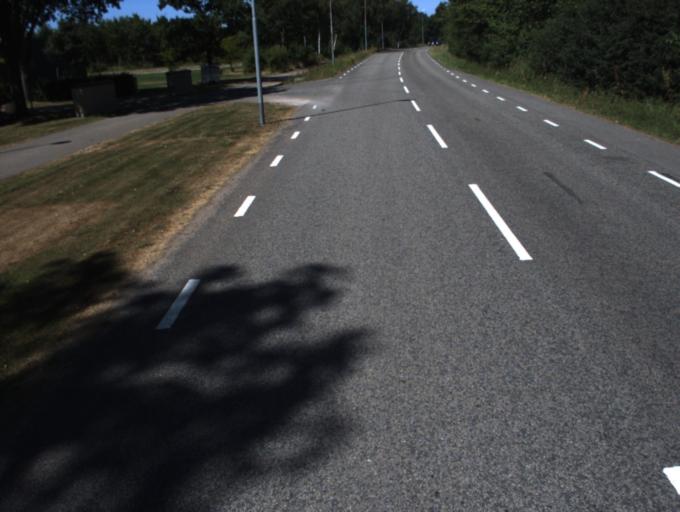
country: SE
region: Skane
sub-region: Helsingborg
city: Helsingborg
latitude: 56.0729
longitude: 12.6927
